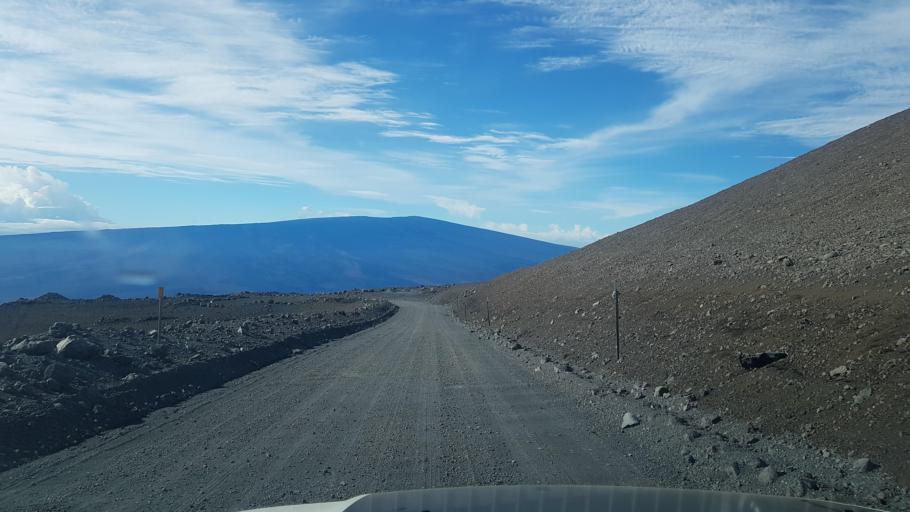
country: US
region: Hawaii
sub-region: Hawaii County
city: Honoka'a
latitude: 19.7815
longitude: -155.4541
